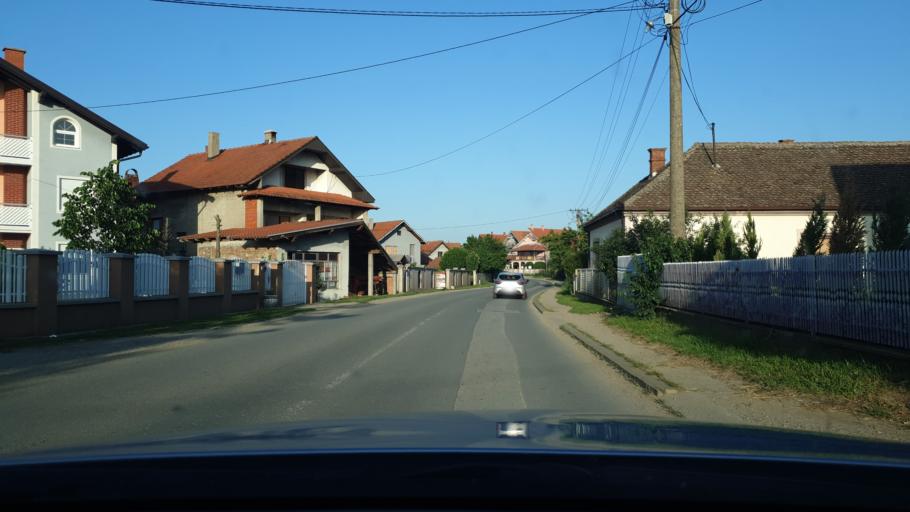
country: RS
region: Central Serbia
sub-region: Podunavski Okrug
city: Velika Plana
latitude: 44.3422
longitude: 21.0863
